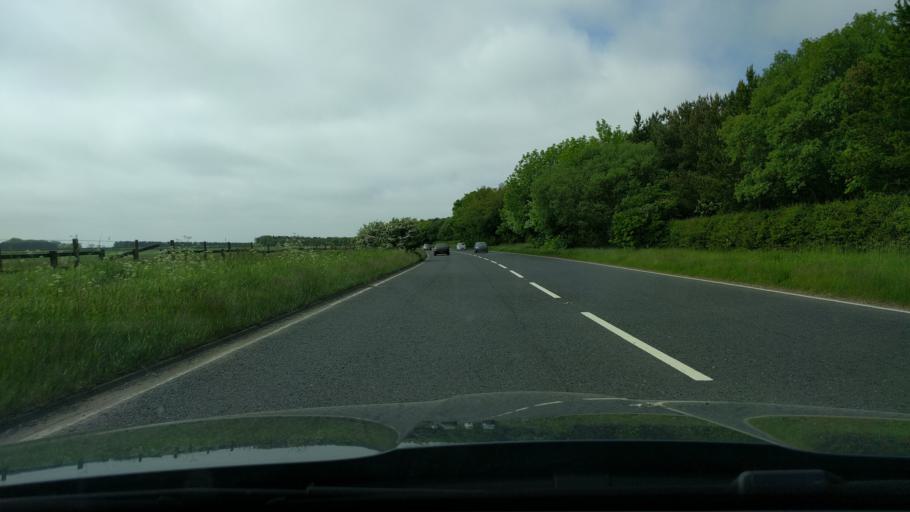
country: GB
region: England
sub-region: Northumberland
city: East Chevington
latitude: 55.2709
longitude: -1.6036
